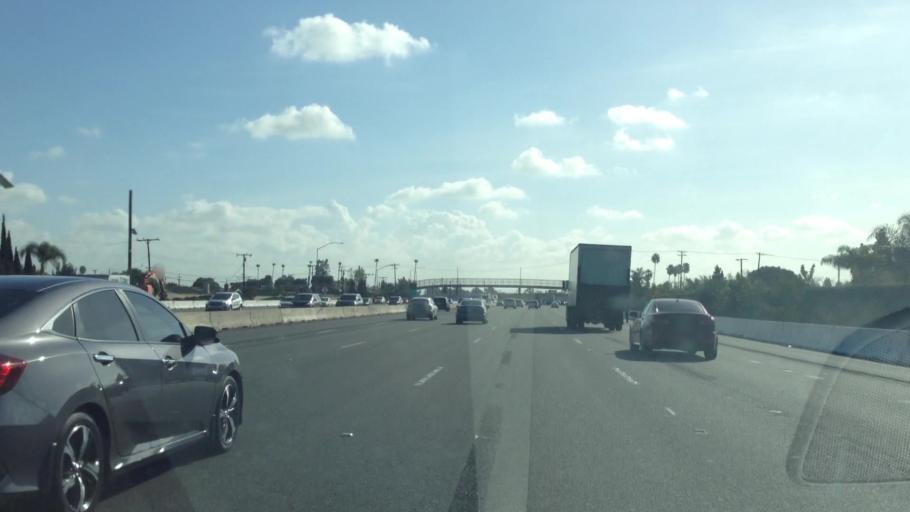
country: US
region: California
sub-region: Orange County
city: Midway City
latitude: 33.7248
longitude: -117.9782
